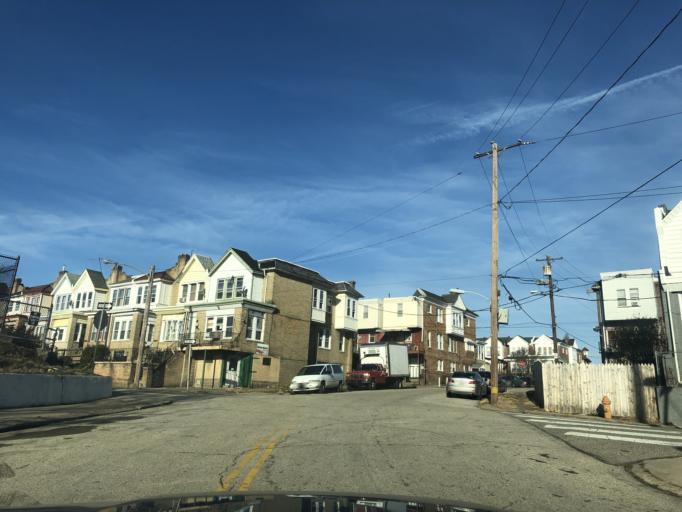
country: US
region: Pennsylvania
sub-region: Montgomery County
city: Bala-Cynwyd
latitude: 39.9857
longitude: -75.2288
